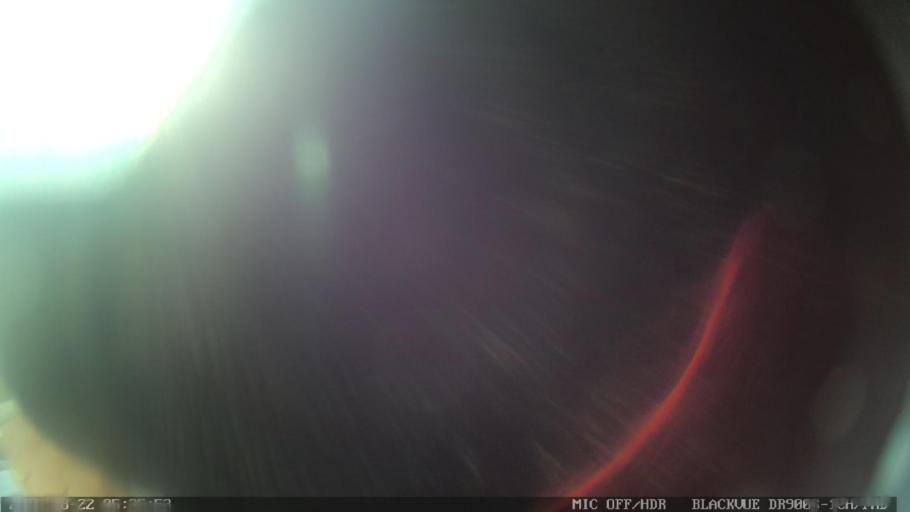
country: PT
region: Castelo Branco
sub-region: Idanha-A-Nova
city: Idanha-a-Nova
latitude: 39.9232
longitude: -7.2377
